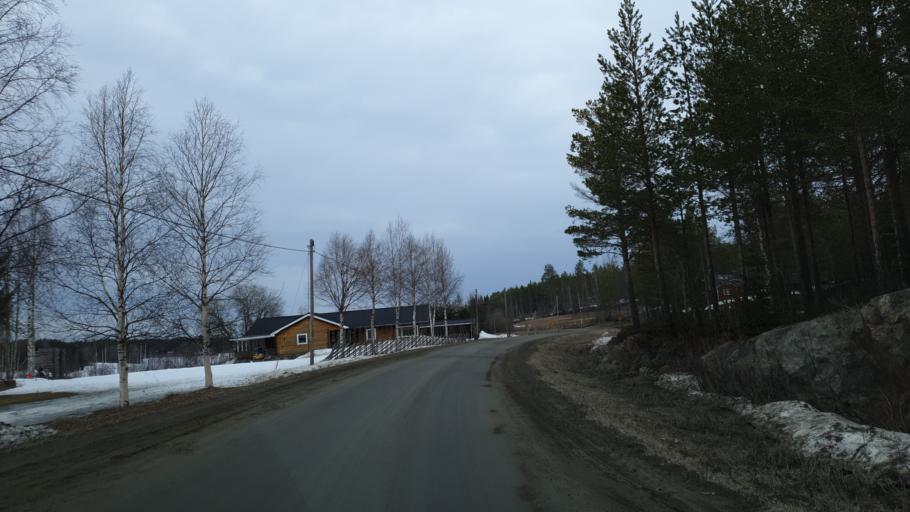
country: SE
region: Vaesterbotten
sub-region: Skelleftea Kommun
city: Burea
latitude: 64.3171
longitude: 21.1387
